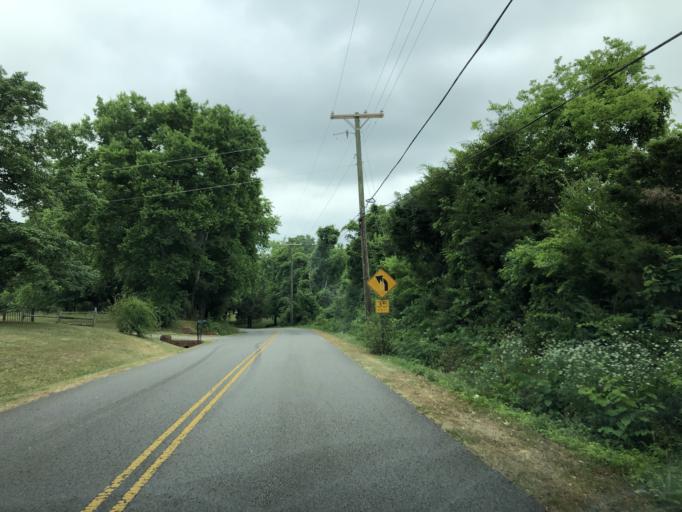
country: US
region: Tennessee
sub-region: Davidson County
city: Goodlettsville
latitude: 36.2828
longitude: -86.7561
